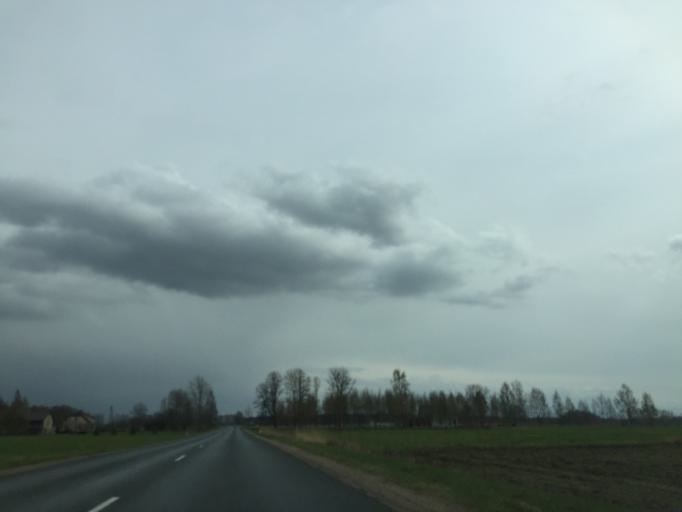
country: LV
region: Cesu Rajons
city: Cesis
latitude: 57.3243
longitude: 25.3137
